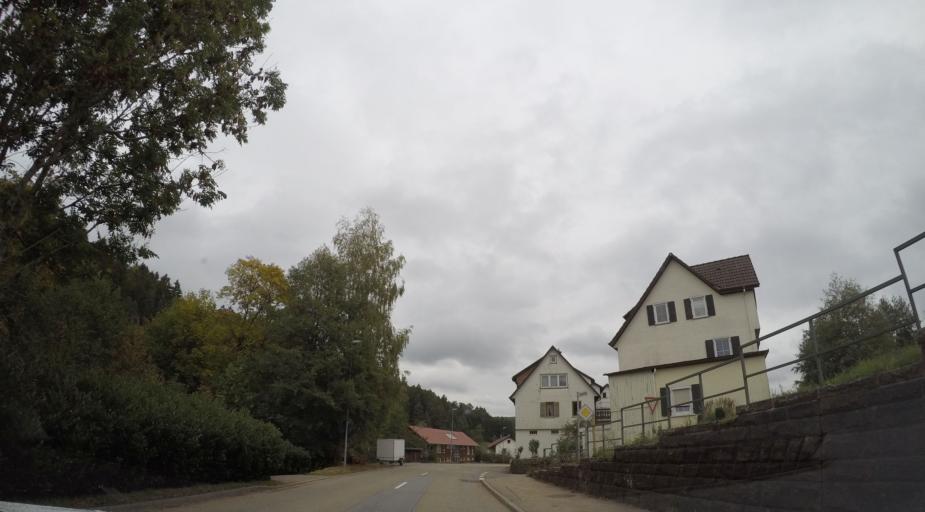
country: DE
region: Baden-Wuerttemberg
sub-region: Karlsruhe Region
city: Baiersbronn
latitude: 48.5238
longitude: 8.3665
